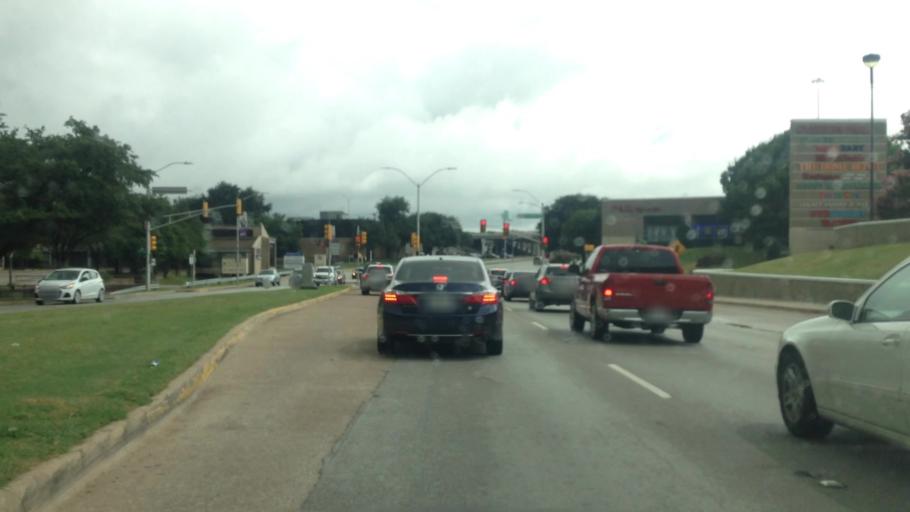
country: US
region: Texas
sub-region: Tarrant County
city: Edgecliff Village
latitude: 32.6836
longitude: -97.3925
